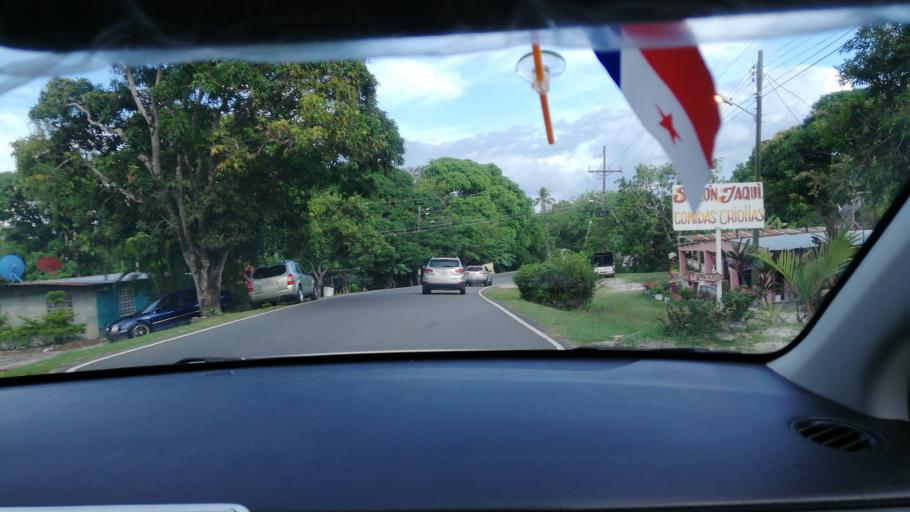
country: PA
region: Panama
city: Las Colinas
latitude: 8.5222
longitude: -80.0374
